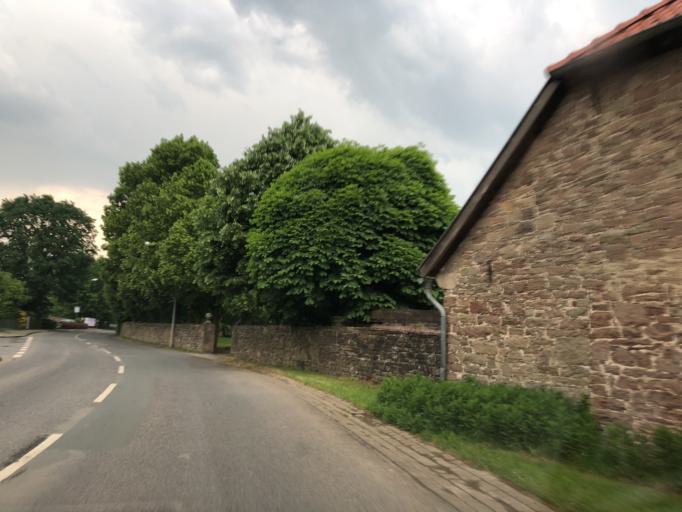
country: DE
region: North Rhine-Westphalia
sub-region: Regierungsbezirk Detmold
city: Dorentrup
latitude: 52.0136
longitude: 9.0181
